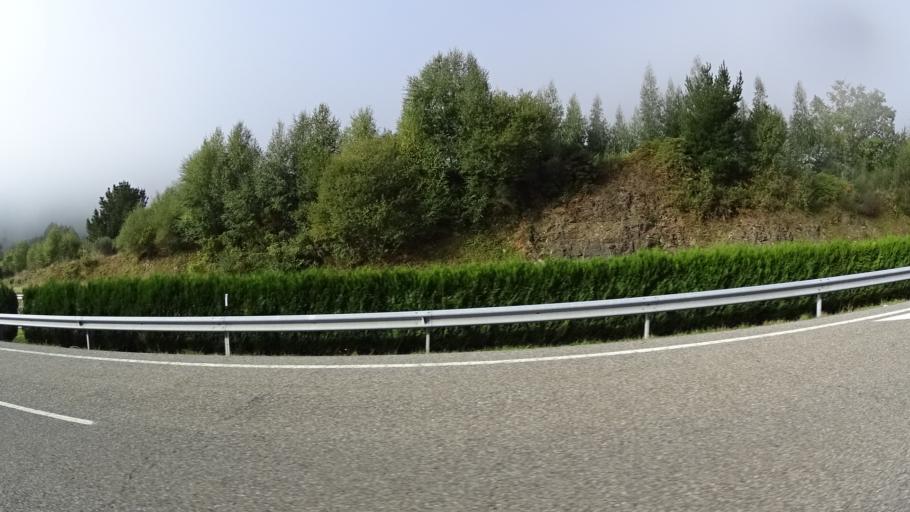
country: ES
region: Galicia
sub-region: Provincia de Lugo
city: Baralla
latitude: 42.9022
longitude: -7.2771
